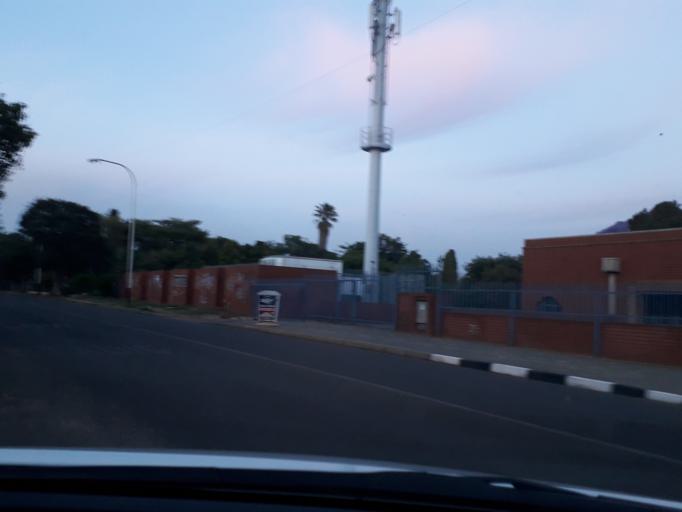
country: ZA
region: Gauteng
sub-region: City of Johannesburg Metropolitan Municipality
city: Johannesburg
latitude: -26.1168
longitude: 28.0009
